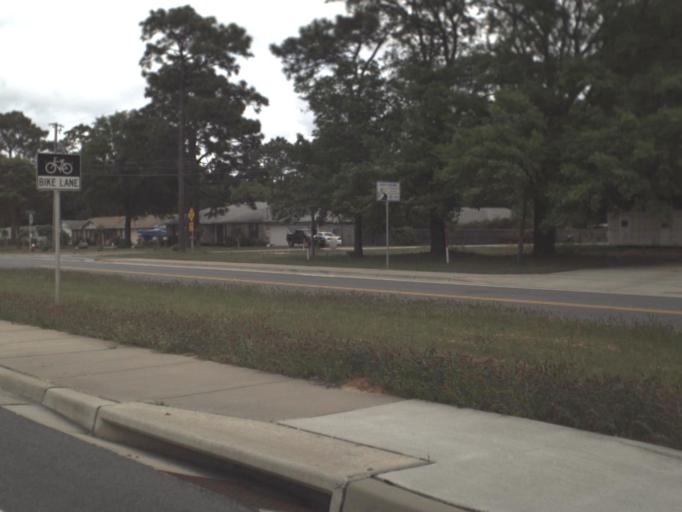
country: US
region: Florida
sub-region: Santa Rosa County
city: Bagdad
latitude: 30.5759
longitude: -87.0864
